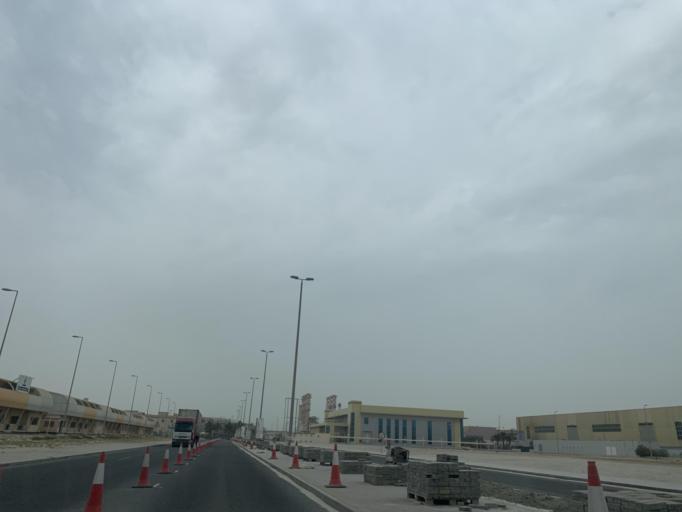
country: BH
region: Muharraq
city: Al Hadd
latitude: 26.2210
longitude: 50.6706
